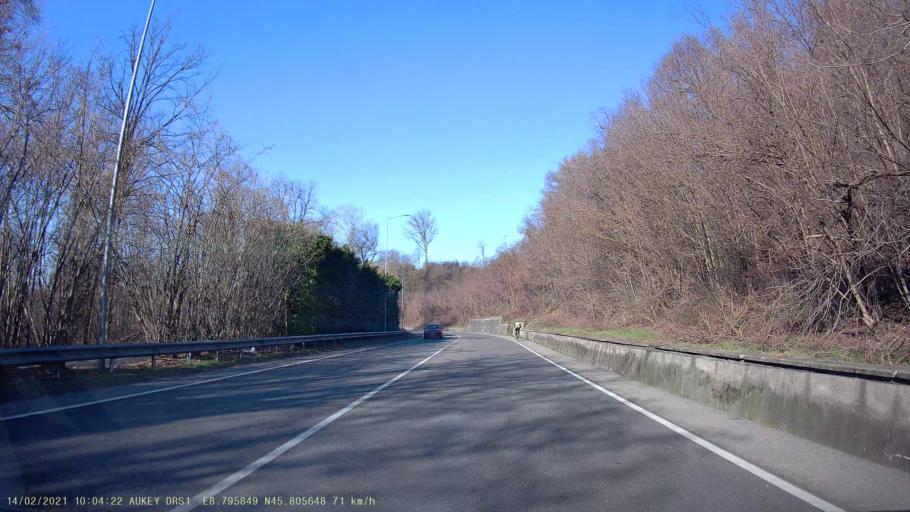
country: IT
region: Lombardy
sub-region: Provincia di Varese
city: Azzate
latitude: 45.8057
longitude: 8.7953
